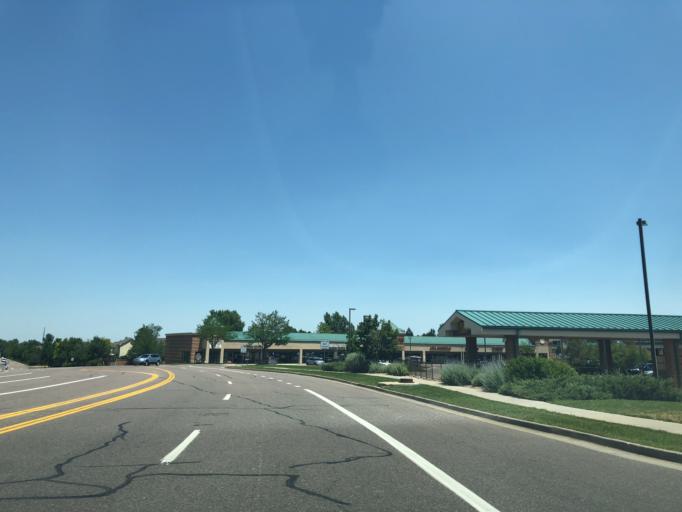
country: US
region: Colorado
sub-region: Arapahoe County
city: Dove Valley
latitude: 39.6185
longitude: -104.7730
